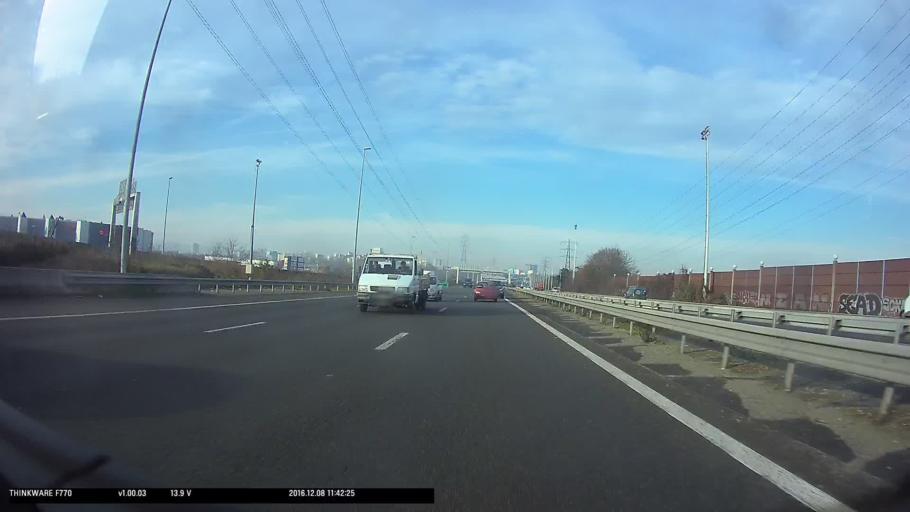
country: FR
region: Ile-de-France
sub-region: Departement du Val-d'Oise
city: Pontoise
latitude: 49.0334
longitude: 2.1055
